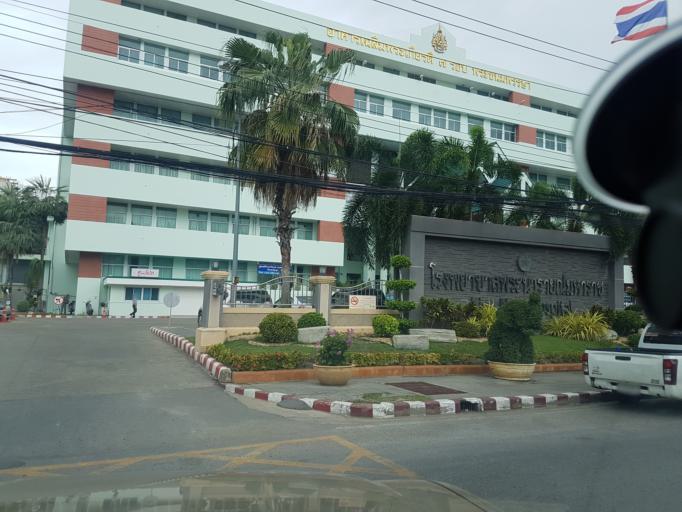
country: TH
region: Lop Buri
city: Lop Buri
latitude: 14.8051
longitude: 100.6519
